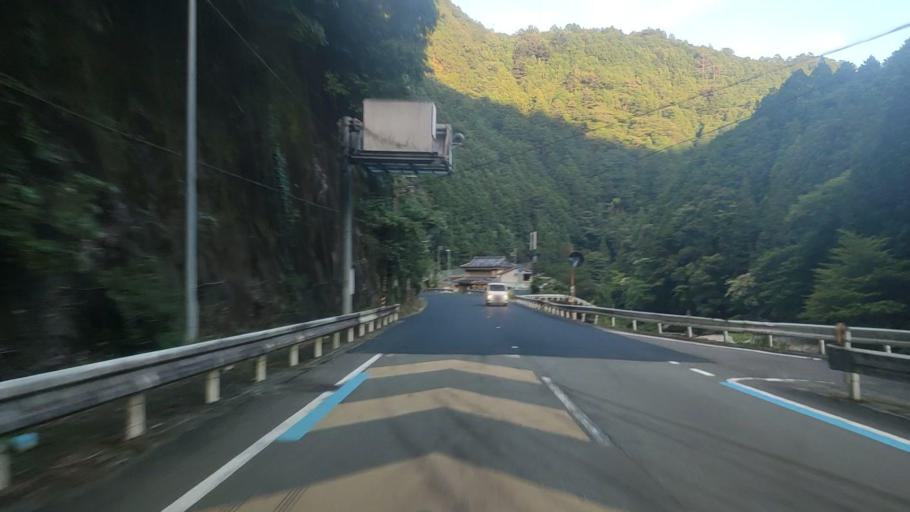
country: JP
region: Wakayama
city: Shingu
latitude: 33.8070
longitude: 135.7116
